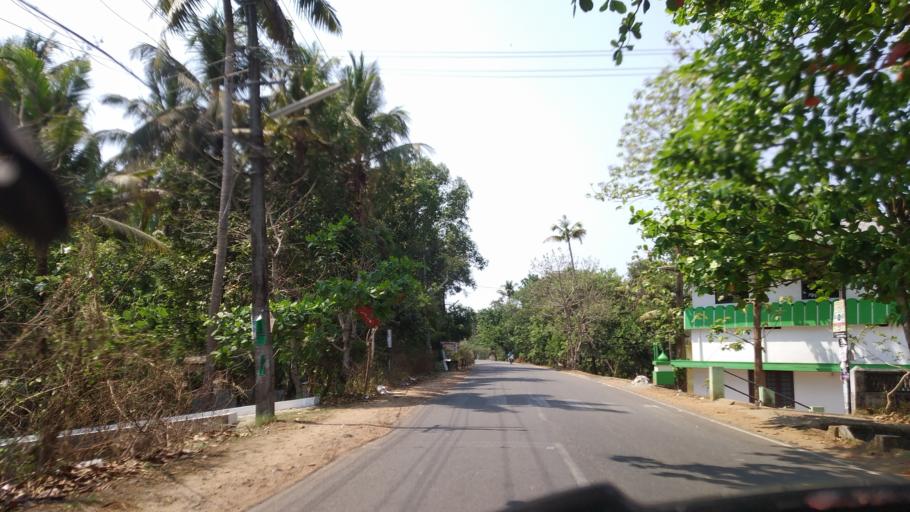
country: IN
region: Kerala
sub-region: Thrissur District
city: Kodungallur
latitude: 10.2029
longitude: 76.1673
